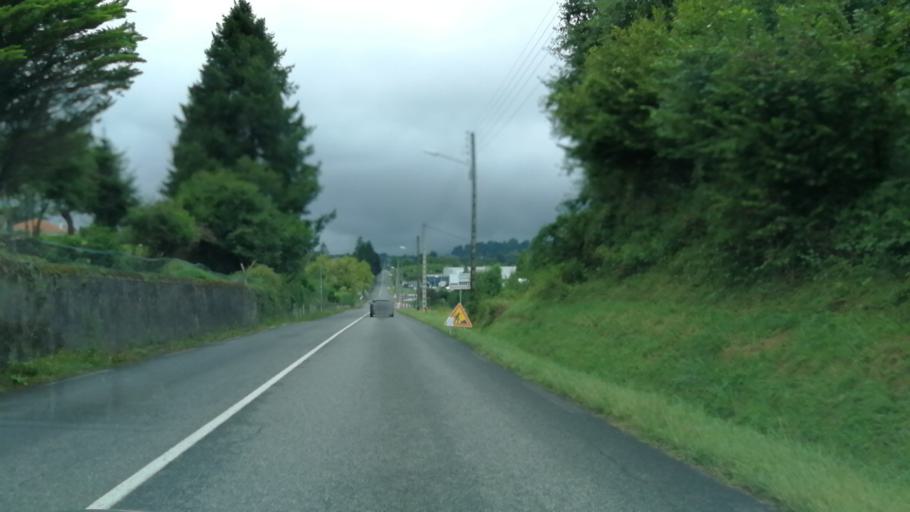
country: FR
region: Aquitaine
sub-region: Departement des Pyrenees-Atlantiques
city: Oloron-Sainte-Marie
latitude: 43.1659
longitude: -0.6012
